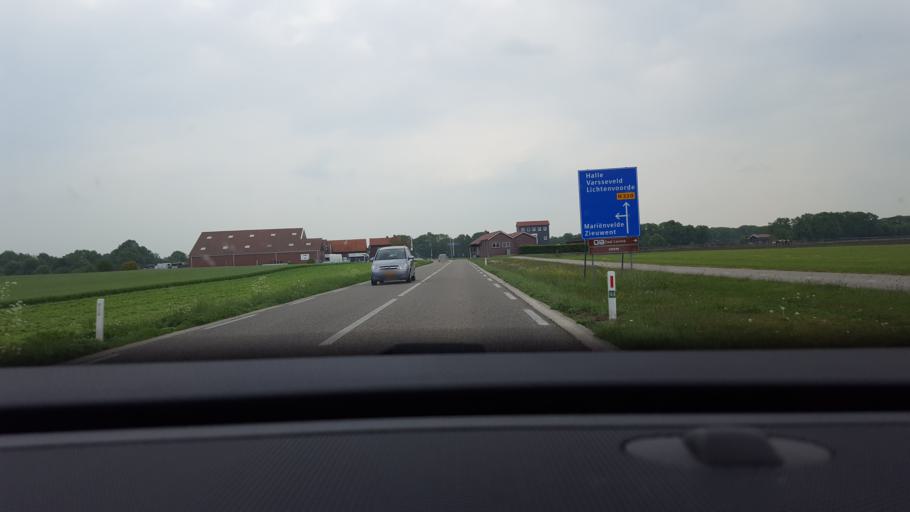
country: NL
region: Gelderland
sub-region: Oude IJsselstreek
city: Varsseveld
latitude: 51.9948
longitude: 6.4171
